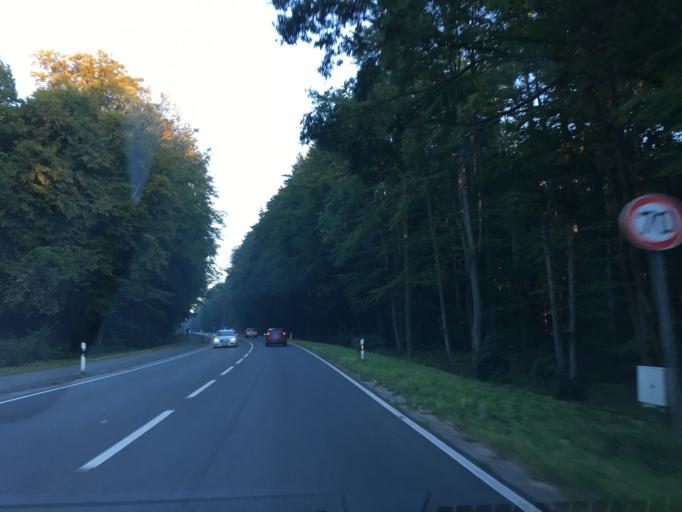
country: DE
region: North Rhine-Westphalia
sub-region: Regierungsbezirk Munster
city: Steinfurt
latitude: 52.1411
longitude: 7.3611
